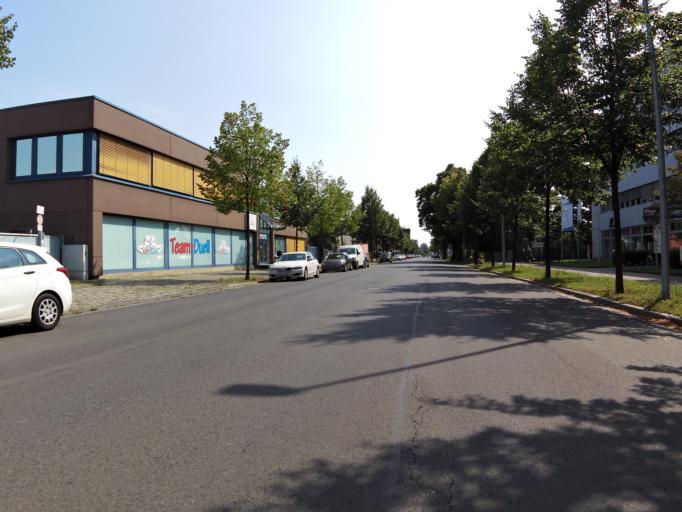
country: DE
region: Saxony
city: Leipzig
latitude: 51.3800
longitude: 12.3932
